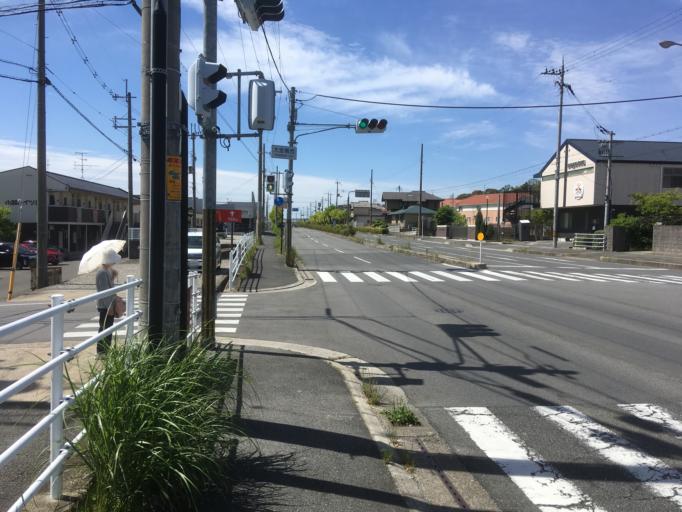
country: JP
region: Nara
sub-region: Ikoma-shi
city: Ikoma
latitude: 34.6769
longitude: 135.7064
